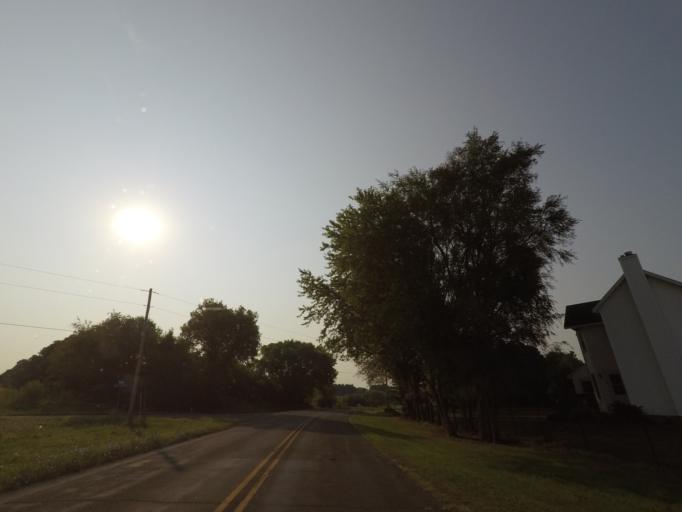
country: US
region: Wisconsin
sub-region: Dane County
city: Cottage Grove
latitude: 43.0426
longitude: -89.2303
